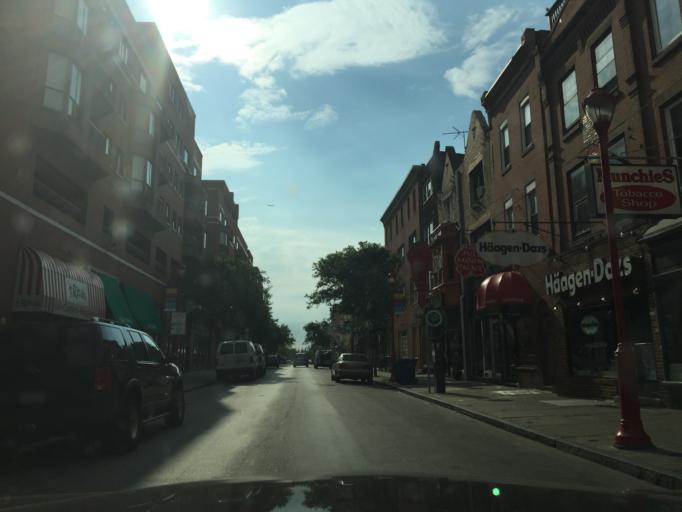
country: US
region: Pennsylvania
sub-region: Philadelphia County
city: Philadelphia
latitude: 39.9414
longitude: -75.1474
